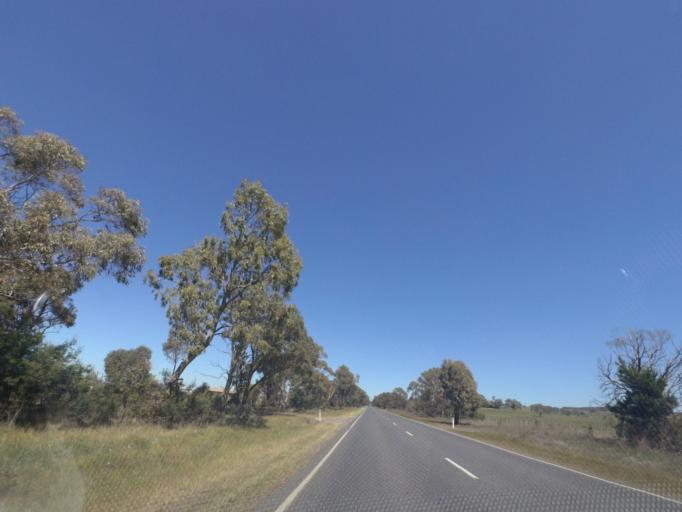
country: AU
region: Victoria
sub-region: Hume
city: Craigieburn
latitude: -37.2955
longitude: 144.8775
